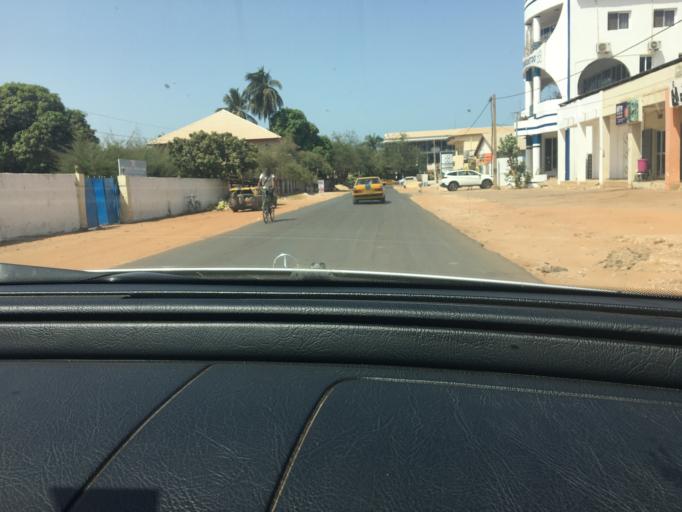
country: GM
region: Banjul
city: Bakau
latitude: 13.4669
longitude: -16.6900
